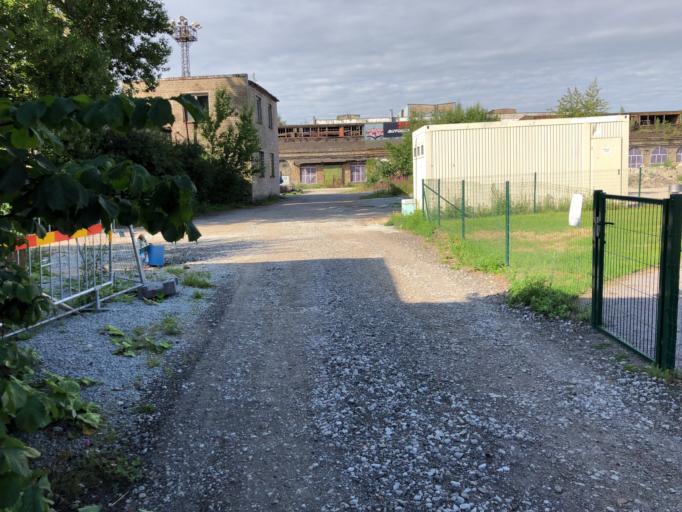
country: EE
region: Harju
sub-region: Tallinna linn
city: Tallinn
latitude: 59.4489
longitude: 24.7236
